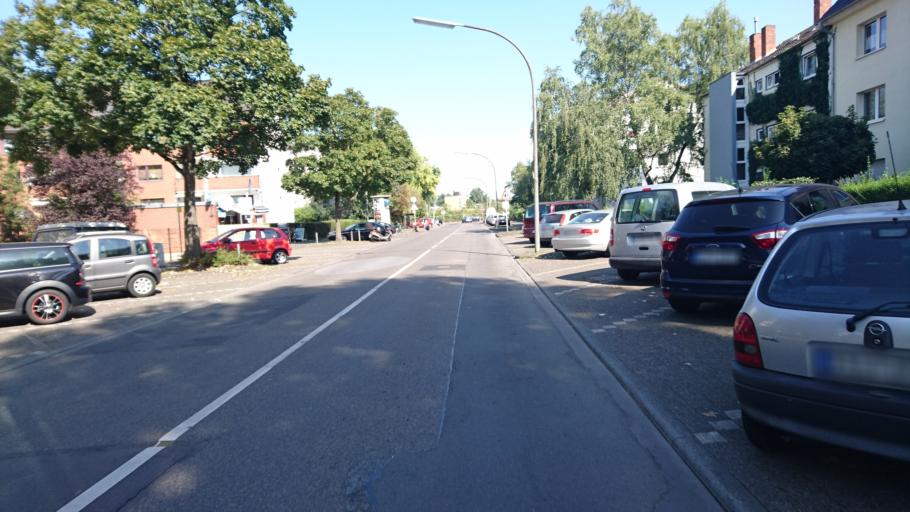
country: DE
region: North Rhine-Westphalia
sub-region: Regierungsbezirk Koln
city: Bilderstoeckchen
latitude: 50.9745
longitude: 6.9284
